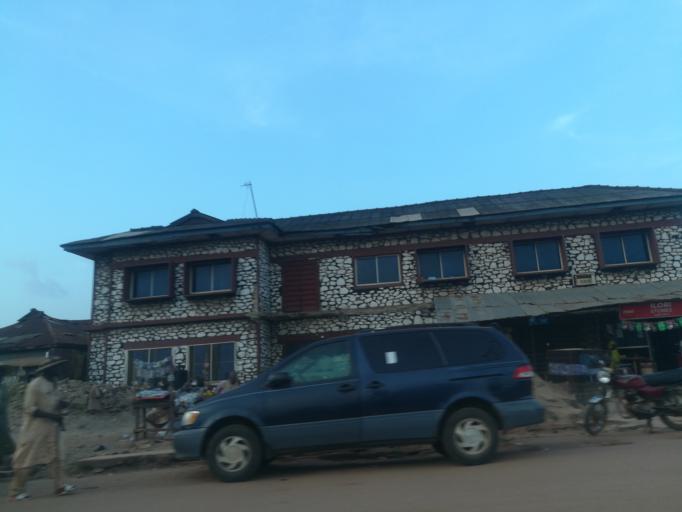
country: NG
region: Ogun
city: Abeokuta
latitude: 7.1695
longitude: 3.3605
